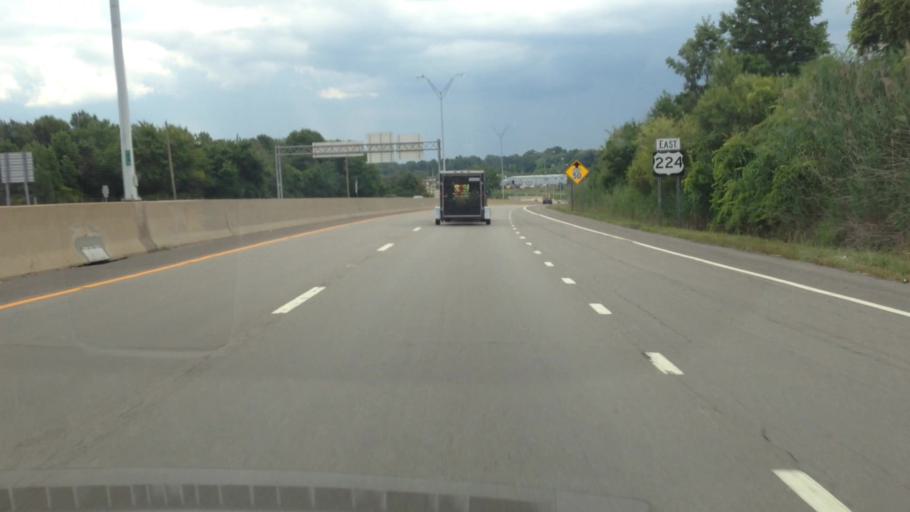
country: US
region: Ohio
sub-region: Summit County
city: Sawyerwood
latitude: 41.0258
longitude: -81.4818
